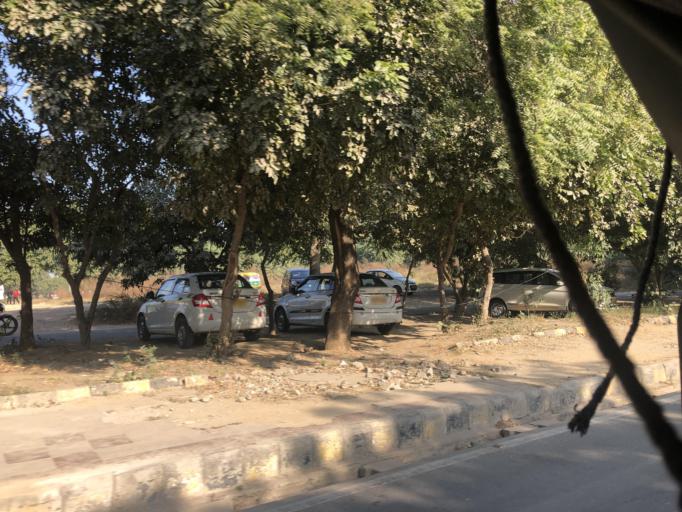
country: IN
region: Haryana
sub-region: Gurgaon
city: Gurgaon
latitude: 28.4628
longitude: 77.0657
